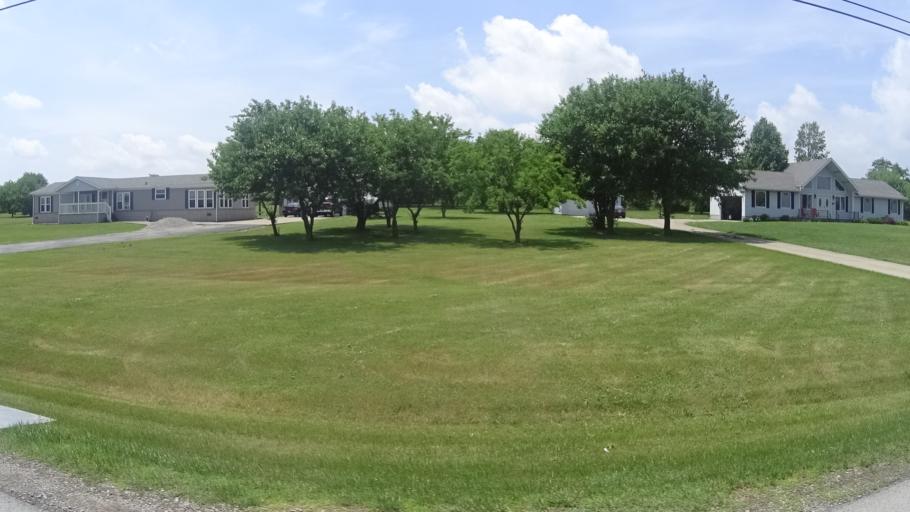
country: US
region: Ohio
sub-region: Erie County
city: Sandusky
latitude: 41.3479
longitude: -82.7508
